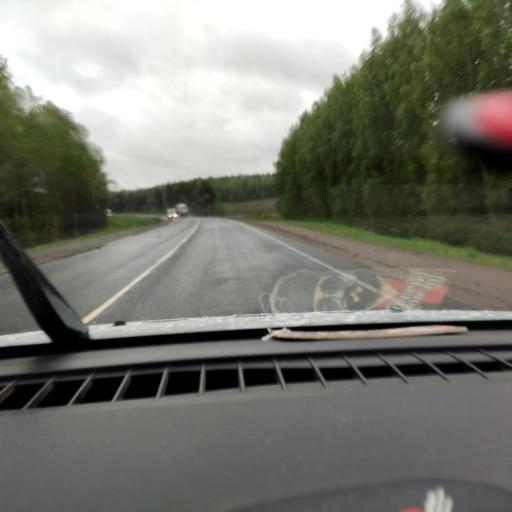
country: RU
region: Perm
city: Kukushtan
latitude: 57.4875
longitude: 56.6681
